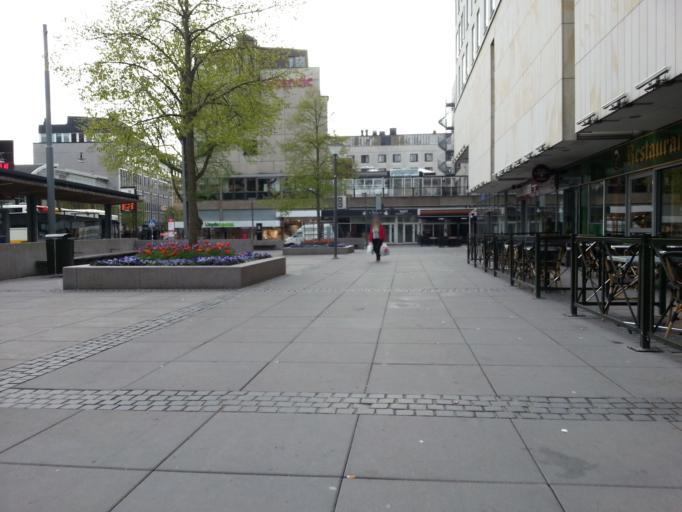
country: SE
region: Joenkoeping
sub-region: Jonkopings Kommun
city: Jonkoping
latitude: 57.7835
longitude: 14.1609
